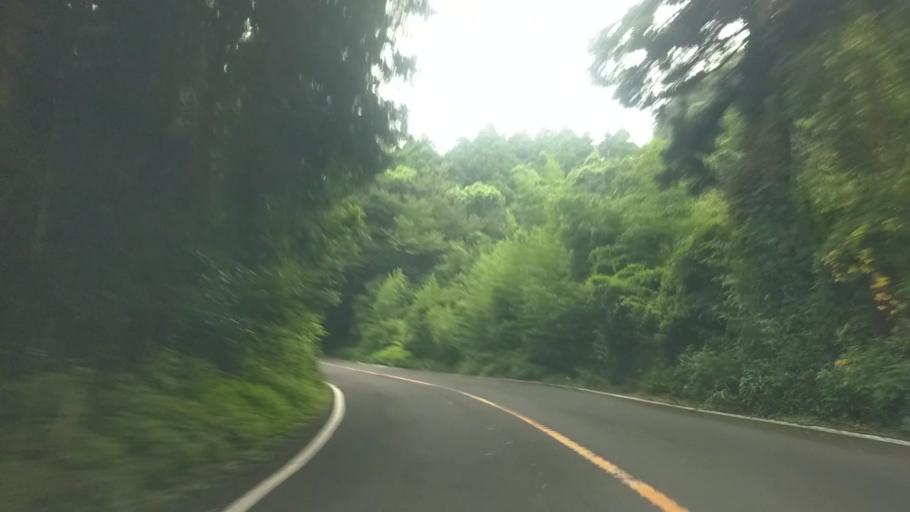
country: JP
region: Chiba
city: Kawaguchi
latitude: 35.2333
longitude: 140.0728
